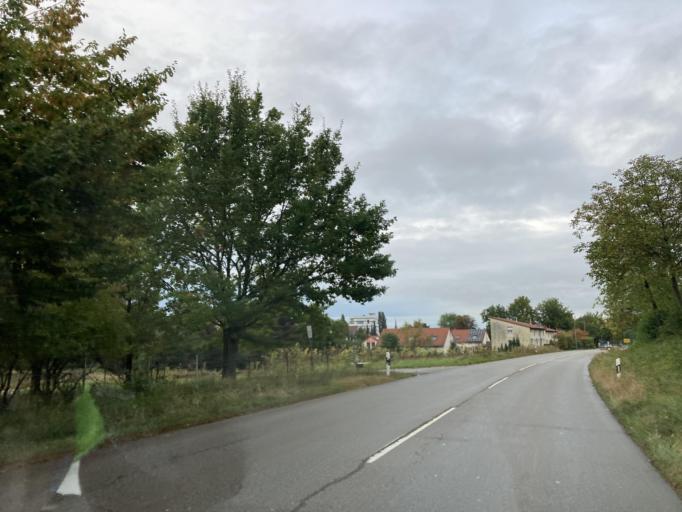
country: DE
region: Baden-Wuerttemberg
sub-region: Freiburg Region
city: Mullheim
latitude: 47.7971
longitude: 7.6226
